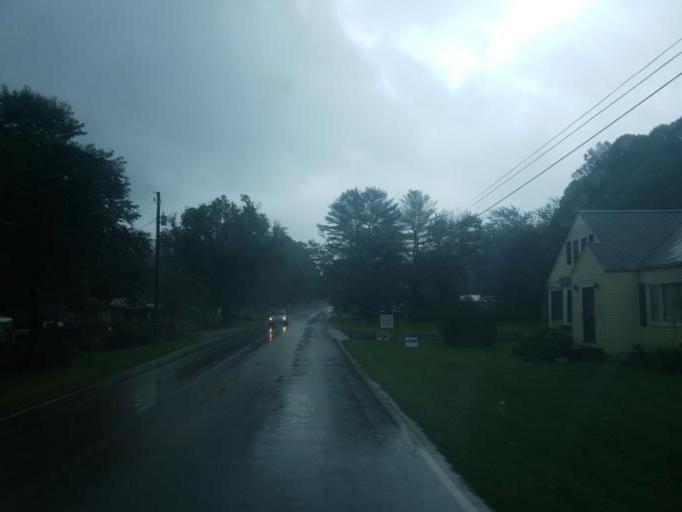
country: US
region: Kentucky
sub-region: Rowan County
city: Morehead
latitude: 38.2353
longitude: -83.3645
